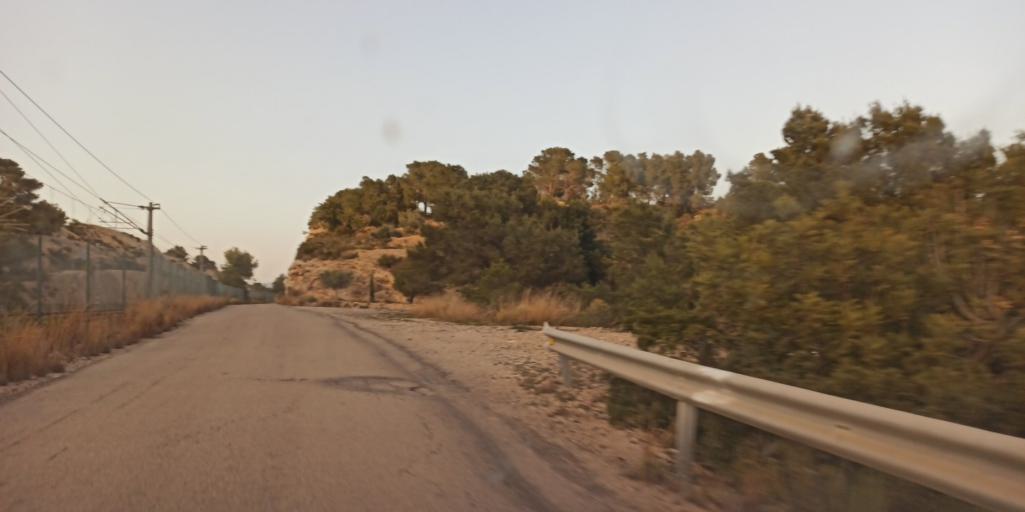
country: ES
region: Catalonia
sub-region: Provincia de Tarragona
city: L'Ampolla
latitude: 40.8394
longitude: 0.7449
